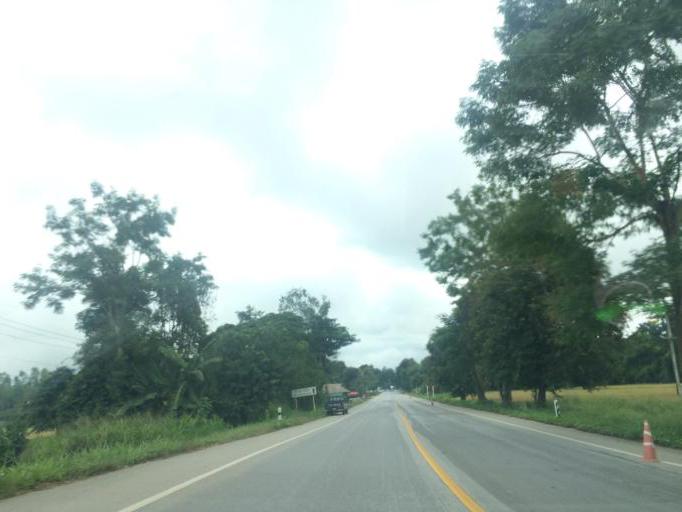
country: TH
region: Chiang Rai
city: Mae Lao
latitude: 19.7476
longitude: 99.6806
